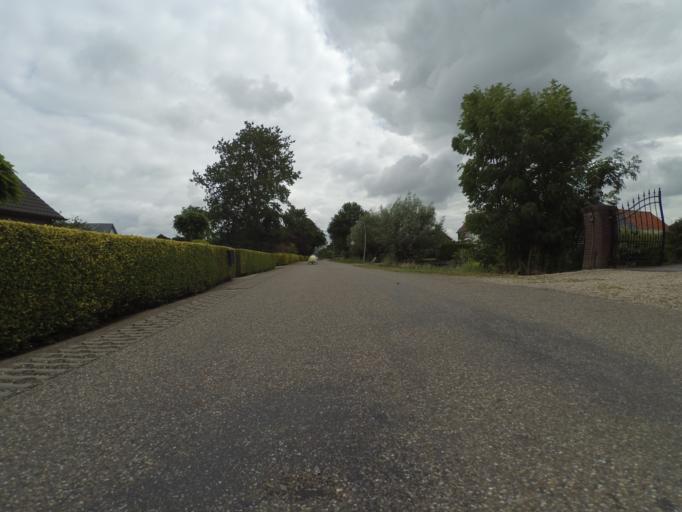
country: NL
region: South Holland
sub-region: Gemeente Leerdam
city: Leerdam
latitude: 51.8911
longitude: 5.0400
